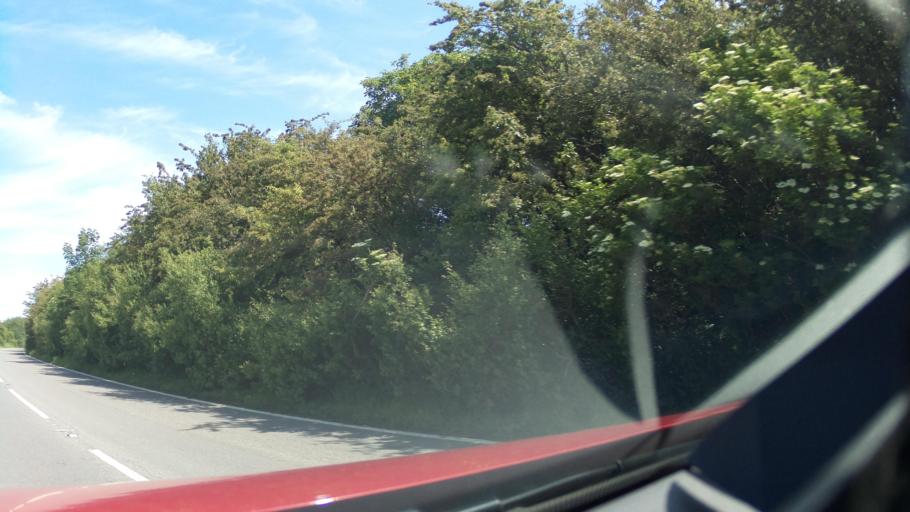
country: GB
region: England
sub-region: North Lincolnshire
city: Manton
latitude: 53.5073
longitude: -0.5828
